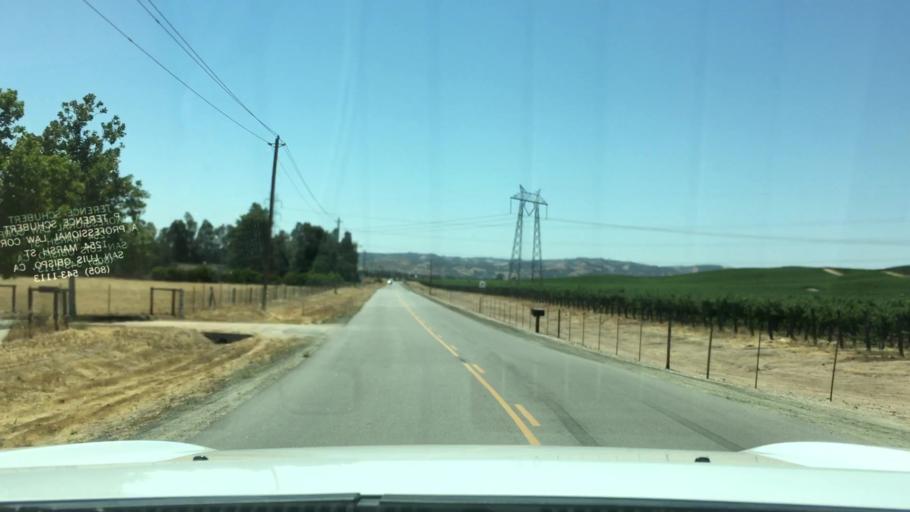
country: US
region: California
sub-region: San Luis Obispo County
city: Paso Robles
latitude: 35.6119
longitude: -120.6234
